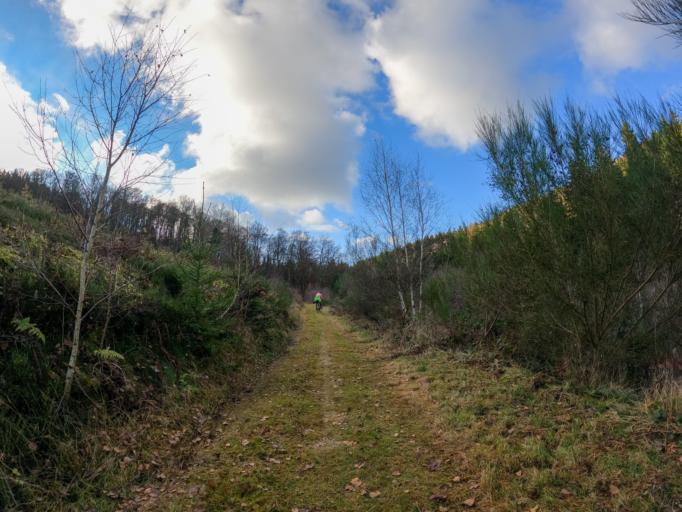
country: LU
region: Diekirch
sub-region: Canton de Wiltz
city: Winseler
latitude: 49.9898
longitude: 5.8465
